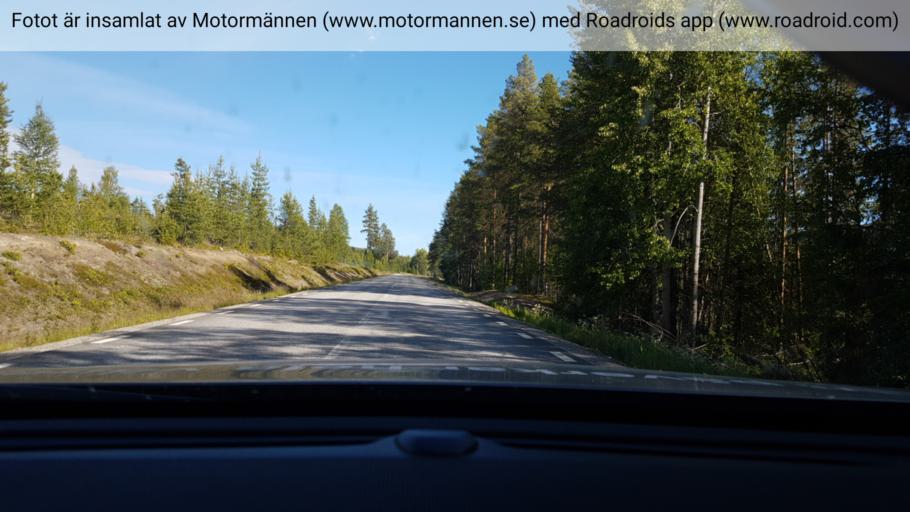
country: SE
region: Vaesterbotten
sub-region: Lycksele Kommun
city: Lycksele
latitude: 64.6805
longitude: 18.4217
